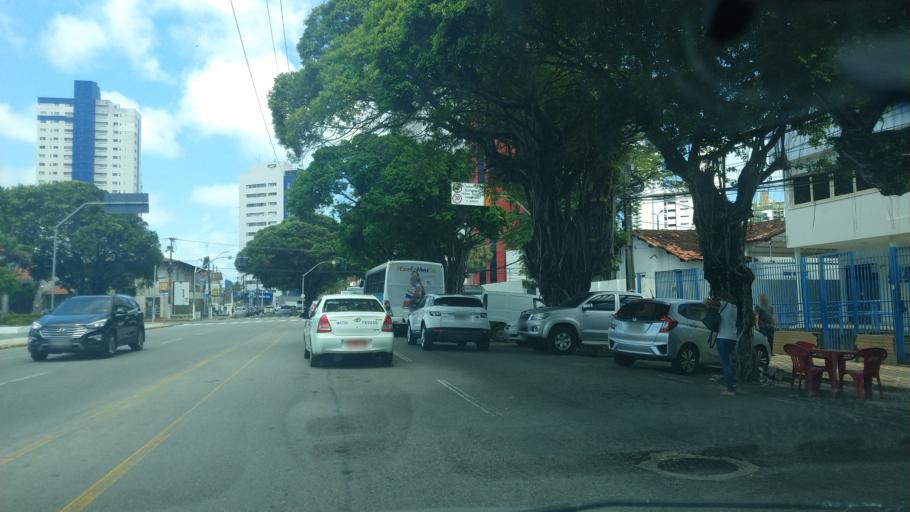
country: BR
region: Rio Grande do Norte
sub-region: Natal
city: Natal
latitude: -5.7848
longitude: -35.2002
